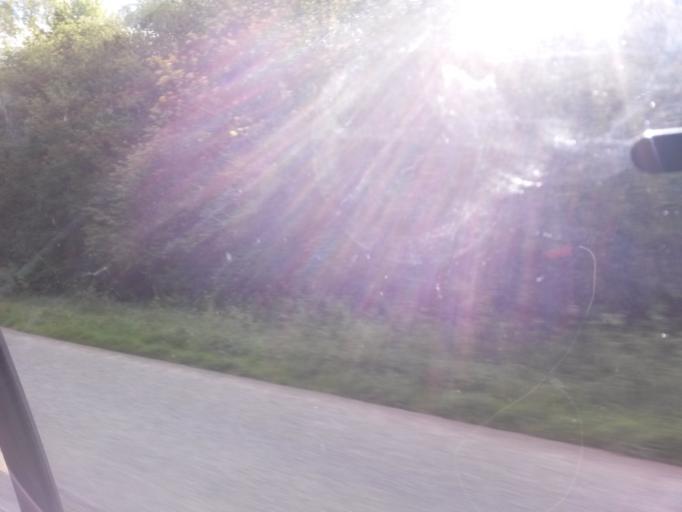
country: IE
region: Leinster
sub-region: Loch Garman
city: Enniscorthy
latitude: 52.5277
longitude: -6.5586
